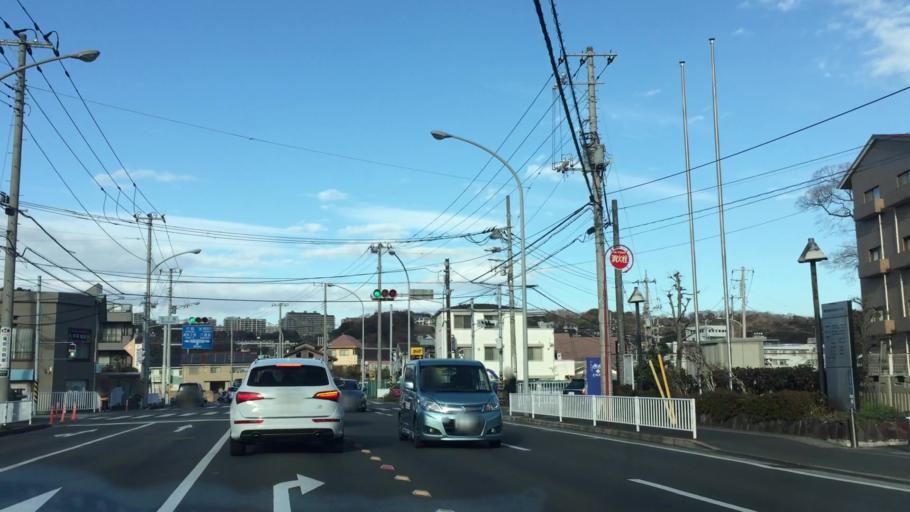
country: JP
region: Kanagawa
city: Zushi
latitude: 35.3421
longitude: 139.6117
